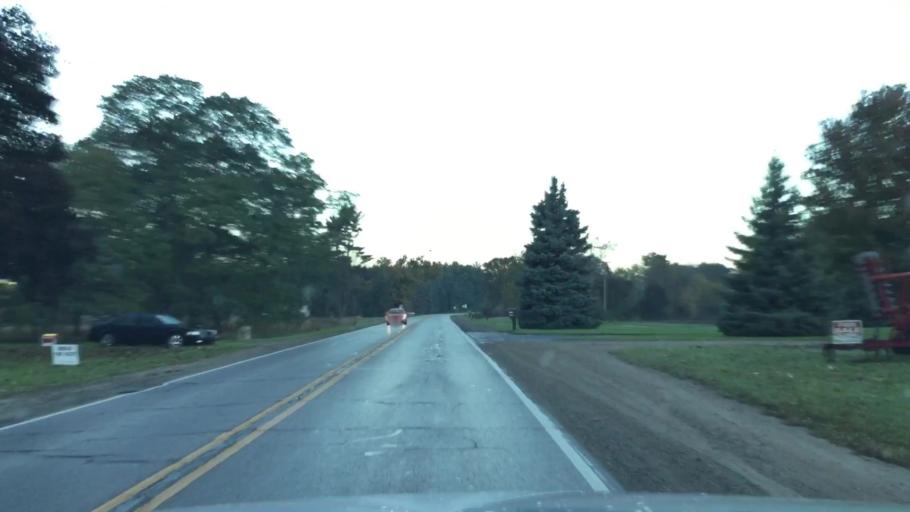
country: US
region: Michigan
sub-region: Livingston County
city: Howell
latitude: 42.6254
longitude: -83.9270
